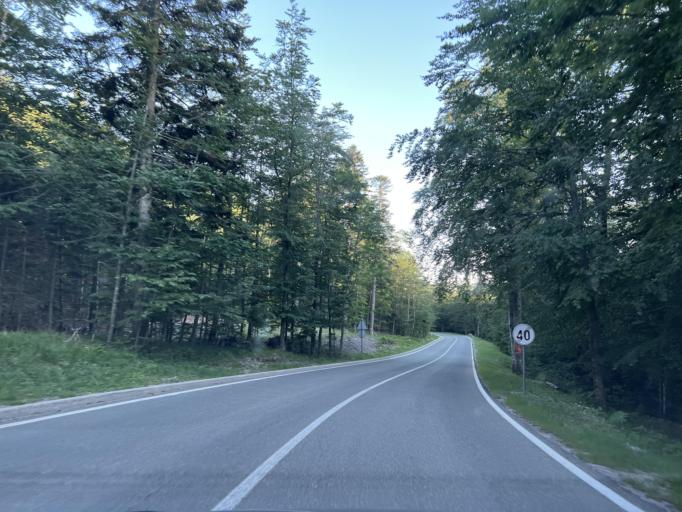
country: HR
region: Primorsko-Goranska
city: Podhum
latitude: 45.4192
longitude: 14.5649
